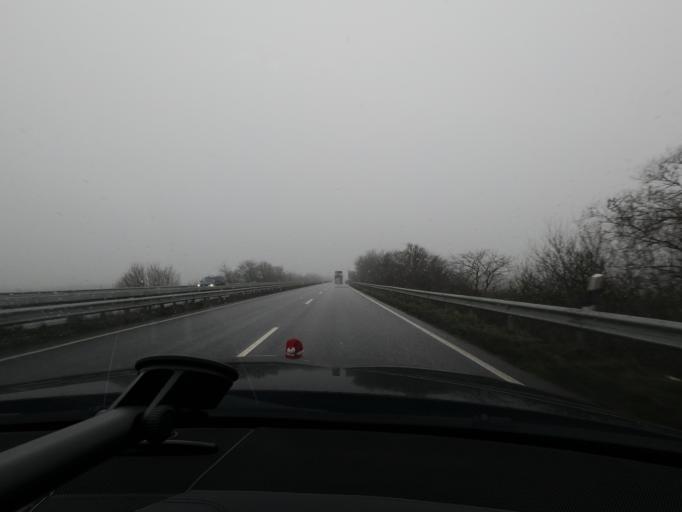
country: DE
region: Schleswig-Holstein
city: Jarplund-Weding
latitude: 54.7380
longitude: 9.4026
